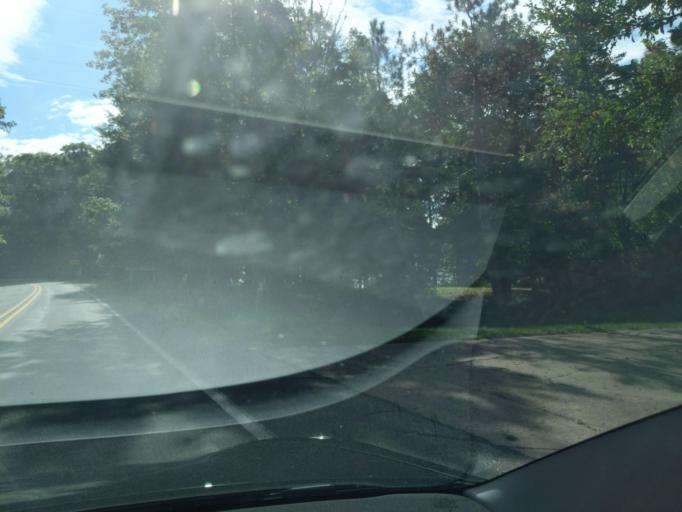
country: US
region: Michigan
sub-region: Antrim County
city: Bellaire
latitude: 45.0070
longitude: -85.2934
